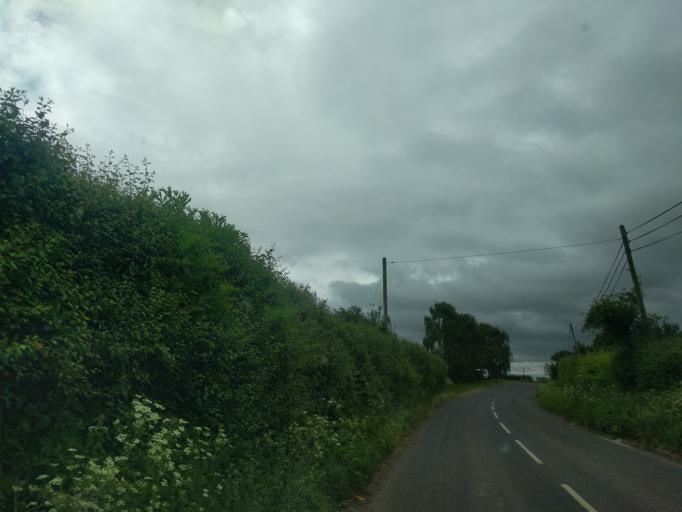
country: GB
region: England
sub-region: Somerset
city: Langport
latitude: 51.0733
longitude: -2.8214
